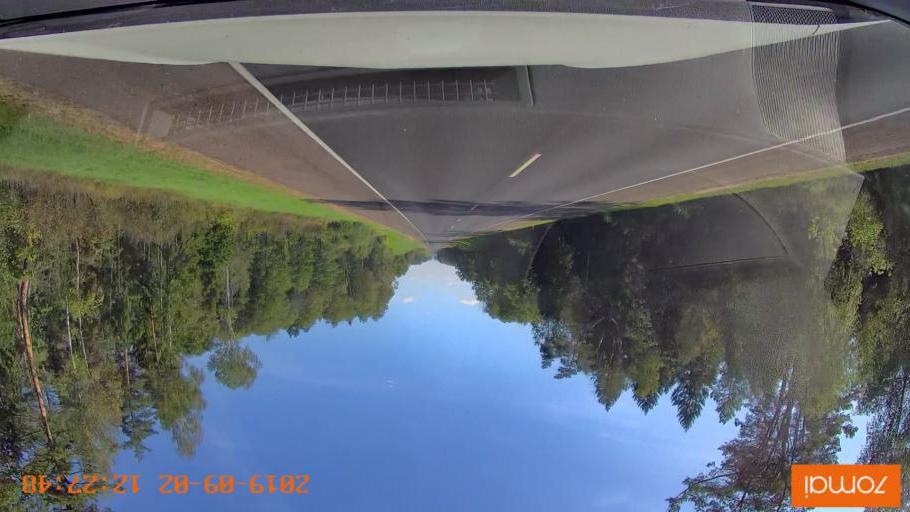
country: RU
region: Smolensk
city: Shumyachi
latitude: 53.8509
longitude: 32.5352
